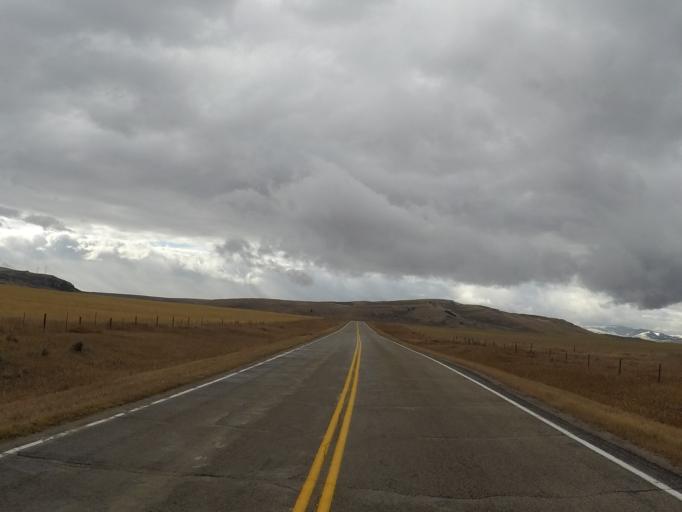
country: US
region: Montana
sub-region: Meagher County
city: White Sulphur Springs
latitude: 46.3383
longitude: -110.7872
